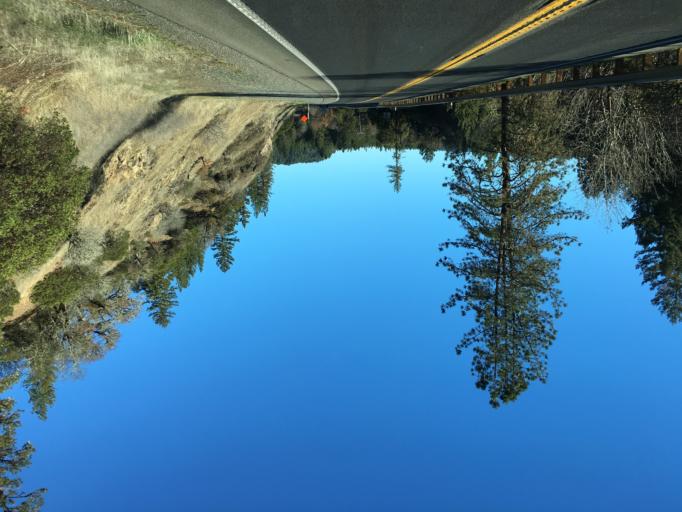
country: US
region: California
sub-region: Mendocino County
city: Laytonville
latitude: 39.7331
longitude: -123.5119
